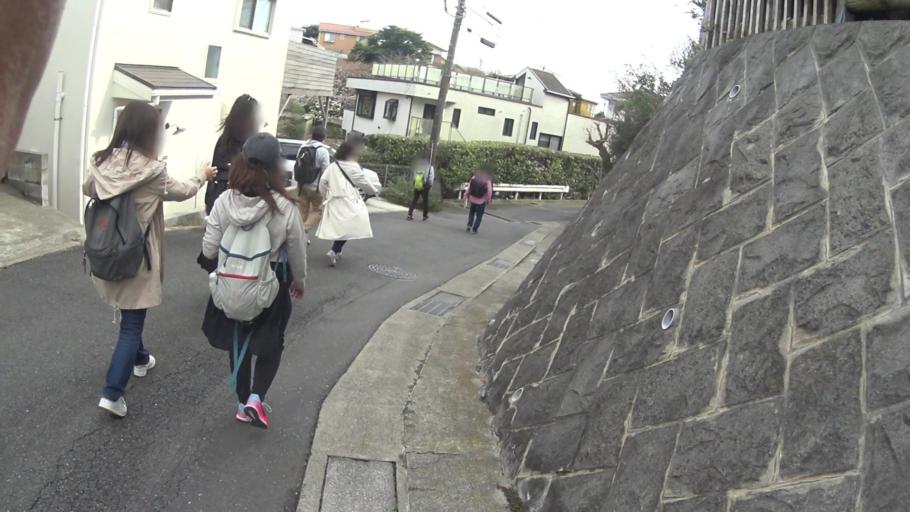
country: JP
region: Kanagawa
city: Kamakura
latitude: 35.3214
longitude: 139.5141
